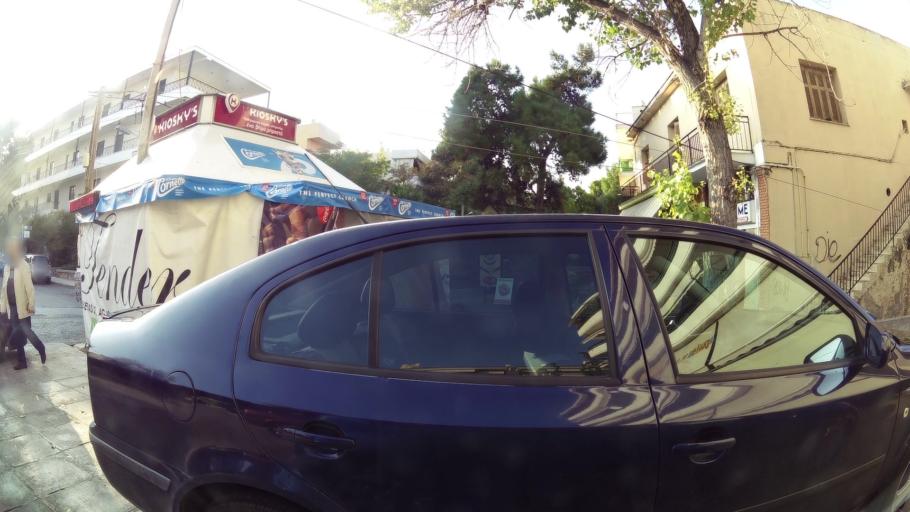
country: GR
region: Attica
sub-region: Nomarchia Athinas
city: Agia Paraskevi
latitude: 38.0066
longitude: 23.8213
